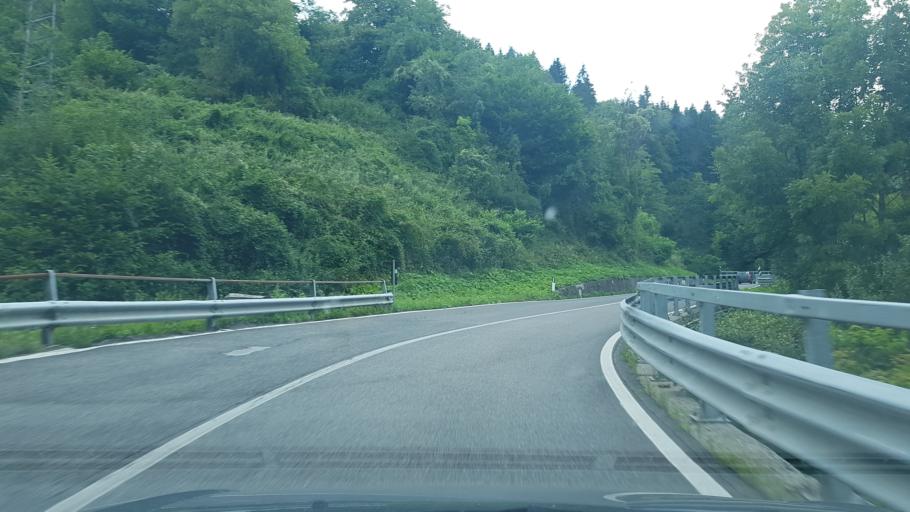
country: IT
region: Friuli Venezia Giulia
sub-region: Provincia di Udine
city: Comeglians
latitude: 46.5218
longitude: 12.8695
